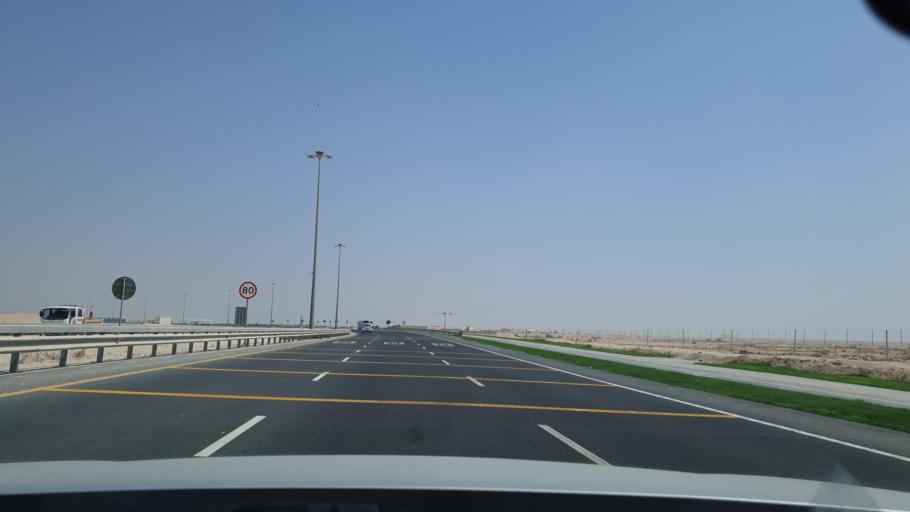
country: QA
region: Baladiyat az Za`ayin
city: Az Za`ayin
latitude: 25.6224
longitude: 51.4092
